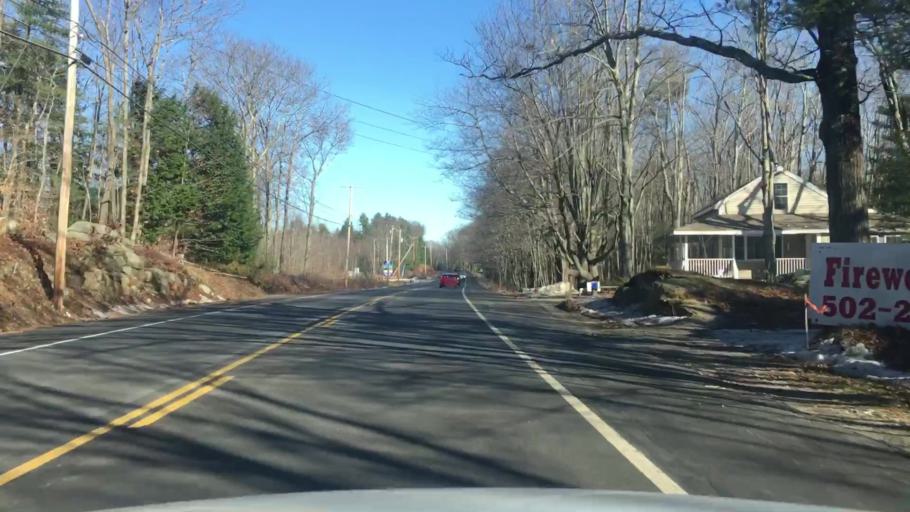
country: US
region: Maine
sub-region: York County
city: Arundel
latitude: 43.4315
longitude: -70.5081
